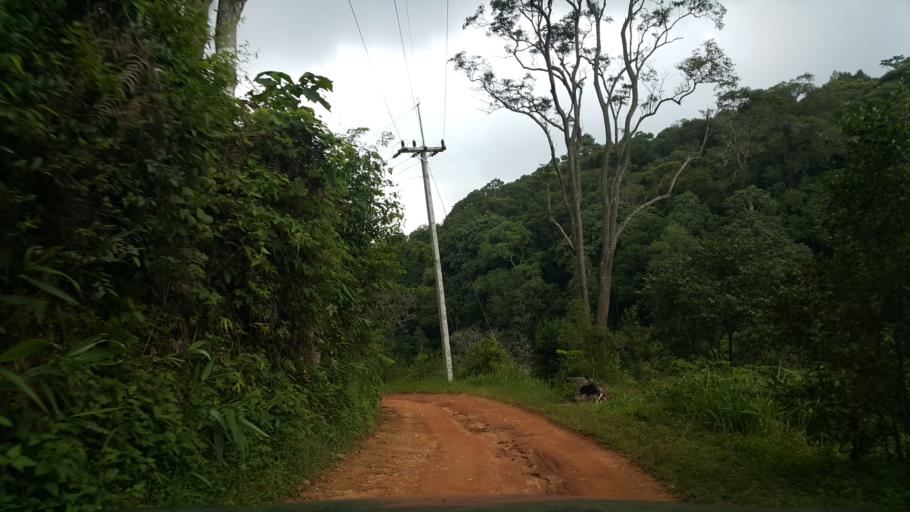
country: TH
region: Lampang
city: Wang Nuea
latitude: 19.1126
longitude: 99.3662
